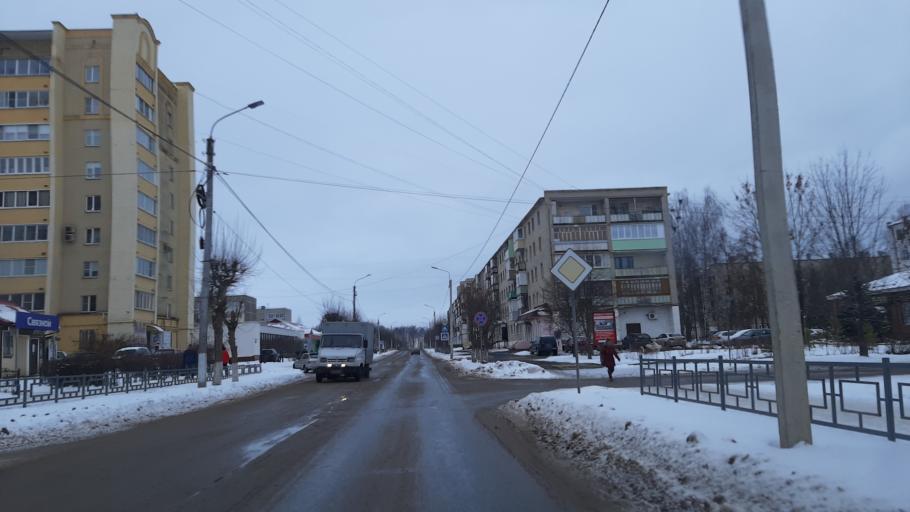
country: RU
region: Kostroma
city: Volgorechensk
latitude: 57.4412
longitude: 41.1528
